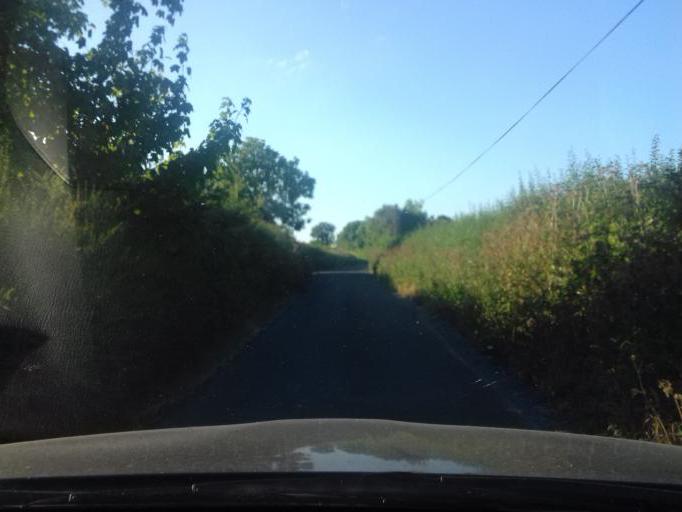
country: IE
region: Leinster
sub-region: An Mhi
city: Ashbourne
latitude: 53.4567
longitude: -6.3853
